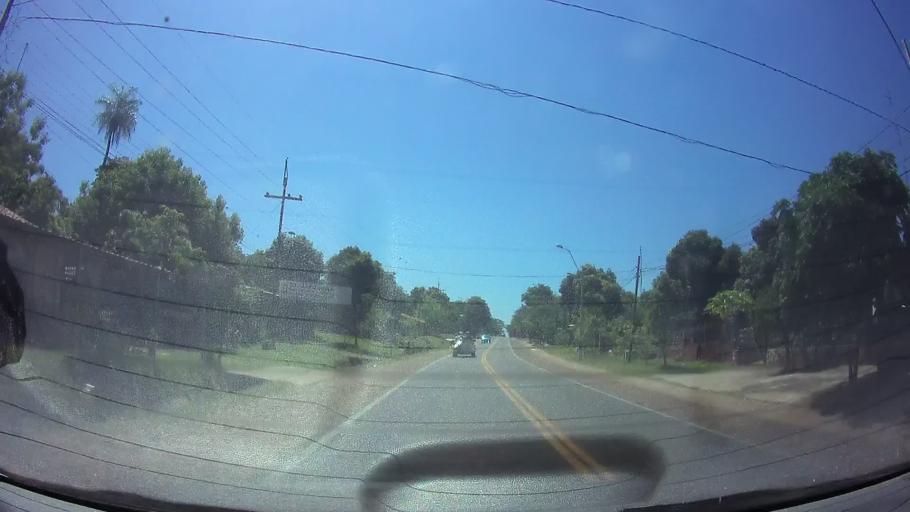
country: PY
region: Central
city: Aregua
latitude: -25.3035
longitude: -57.4023
